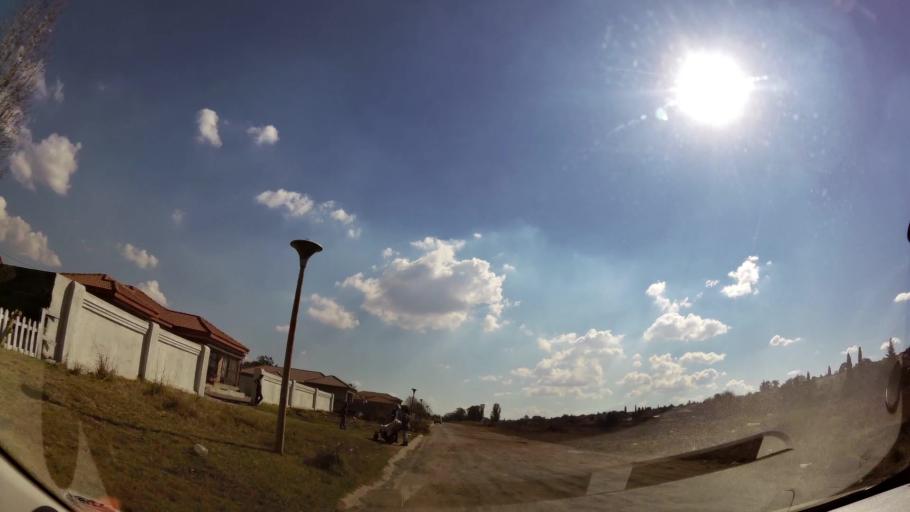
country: ZA
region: Mpumalanga
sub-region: Nkangala District Municipality
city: Witbank
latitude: -25.9367
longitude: 29.2463
